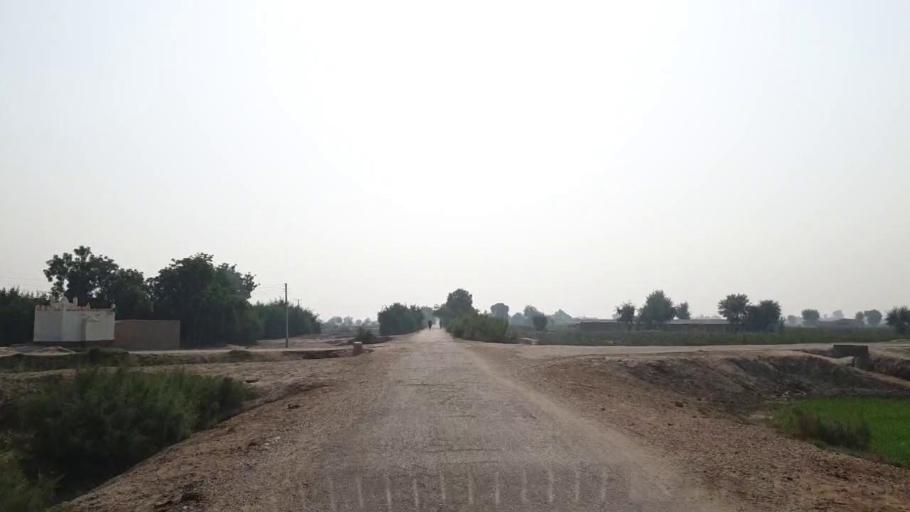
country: PK
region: Sindh
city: Bhan
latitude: 26.4792
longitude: 67.7710
